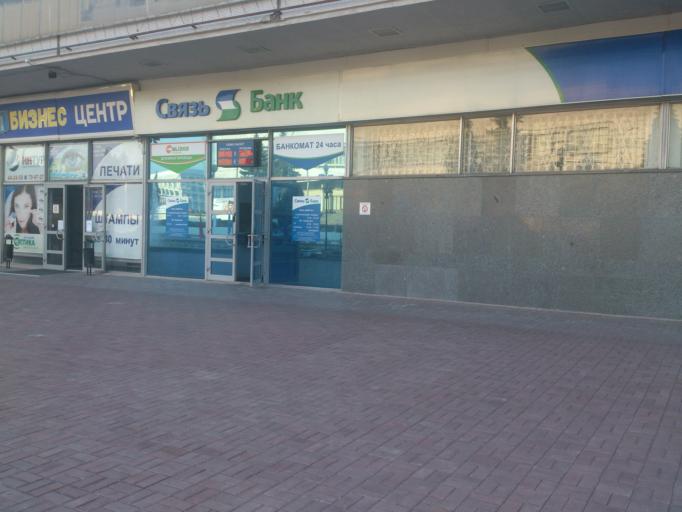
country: RU
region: Ulyanovsk
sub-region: Ulyanovskiy Rayon
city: Ulyanovsk
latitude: 54.3206
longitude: 48.4040
